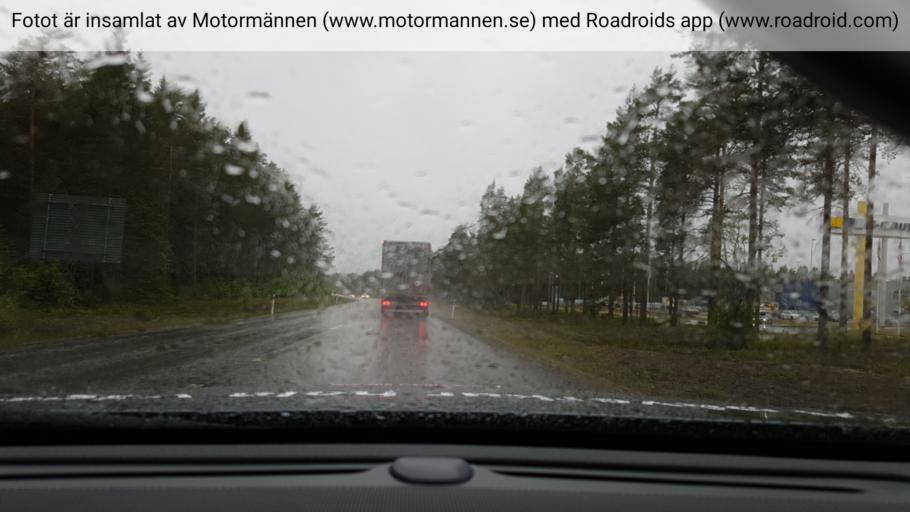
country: SE
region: Vaesterbotten
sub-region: Umea Kommun
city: Roback
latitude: 63.8460
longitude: 20.1556
